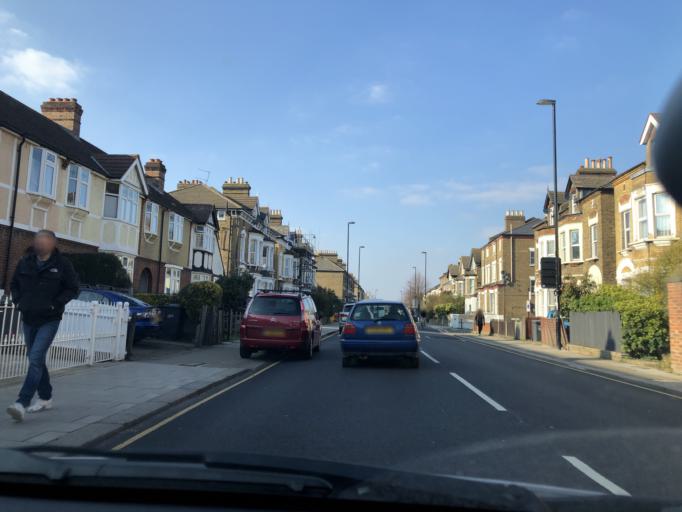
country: GB
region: England
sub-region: Greater London
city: Catford
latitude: 51.4522
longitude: -0.0072
